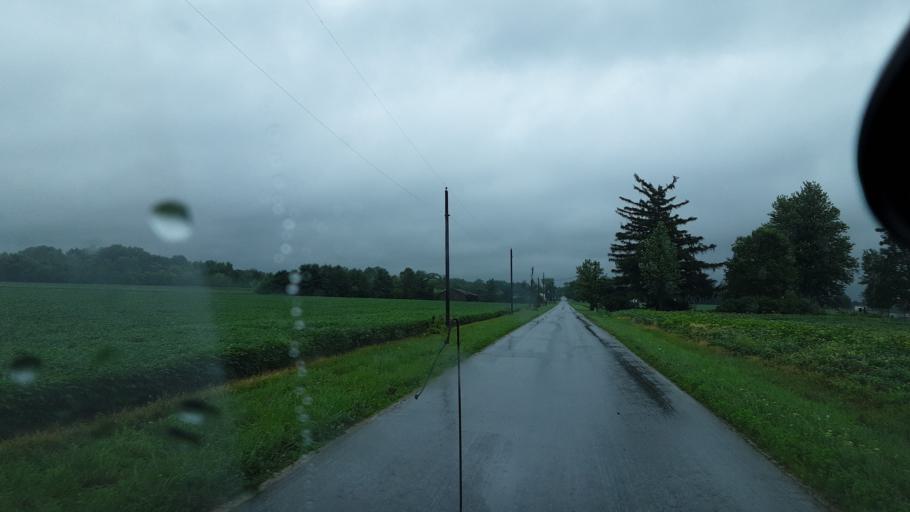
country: US
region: Indiana
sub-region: Adams County
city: Decatur
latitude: 40.7756
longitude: -84.8534
